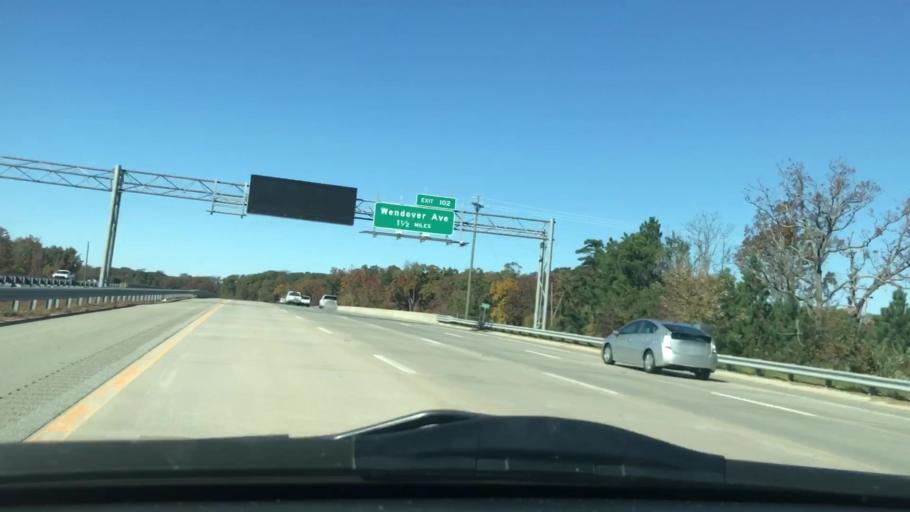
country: US
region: North Carolina
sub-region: Guilford County
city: Jamestown
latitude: 36.0352
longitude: -79.8895
